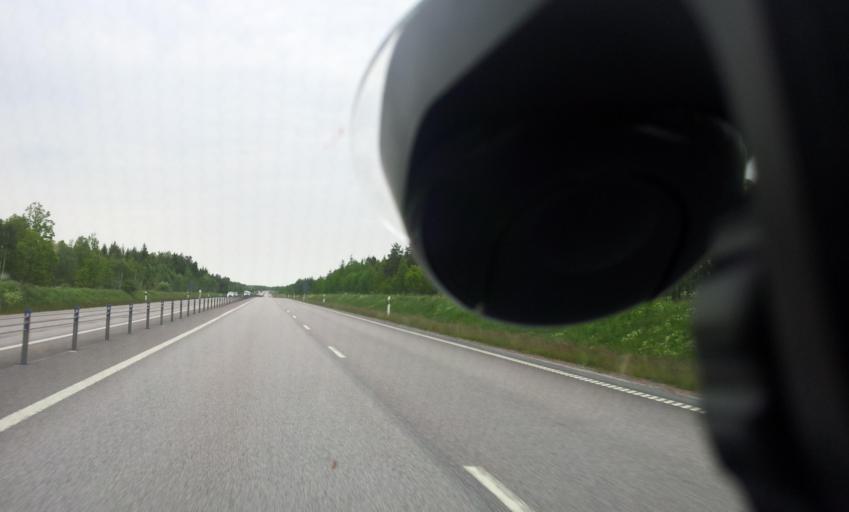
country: SE
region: Kalmar
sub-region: Monsteras Kommun
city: Timmernabben
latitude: 56.9697
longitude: 16.3955
